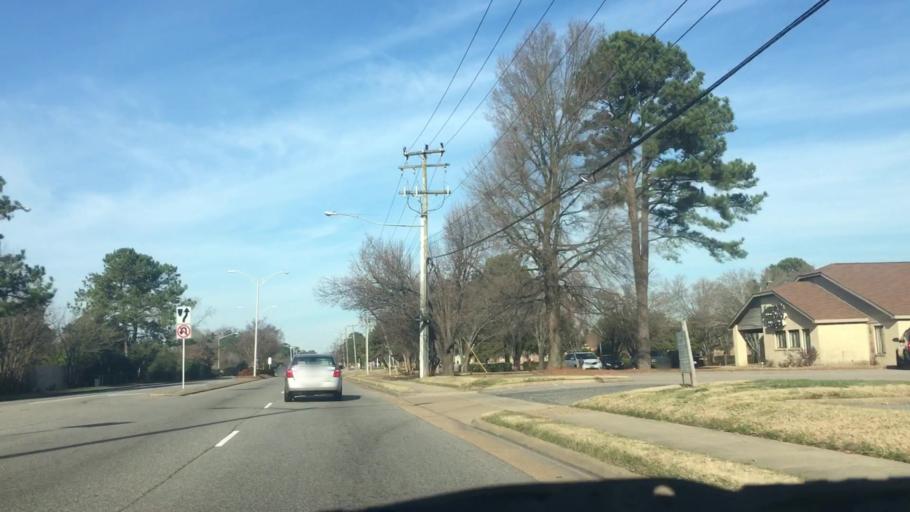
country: US
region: Virginia
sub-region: City of Chesapeake
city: Chesapeake
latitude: 36.8120
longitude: -76.1401
